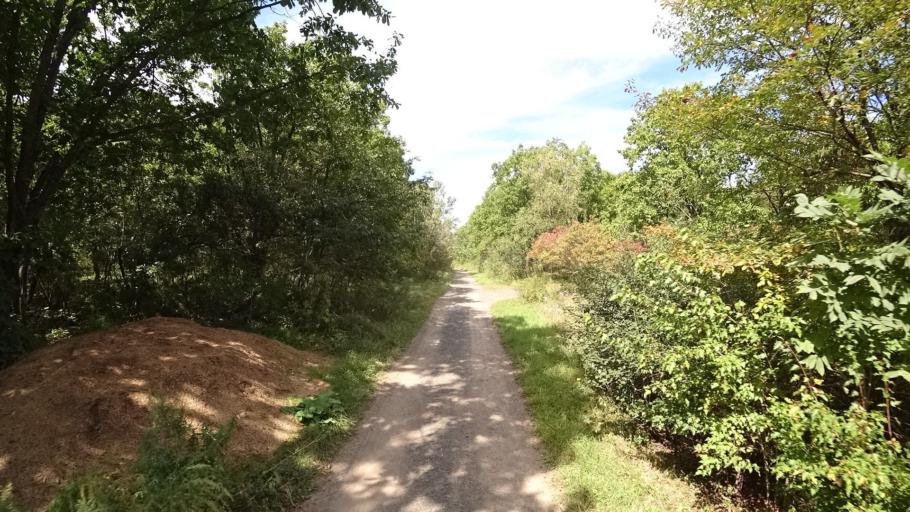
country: RU
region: Primorskiy
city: Yakovlevka
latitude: 44.6493
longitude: 133.5906
